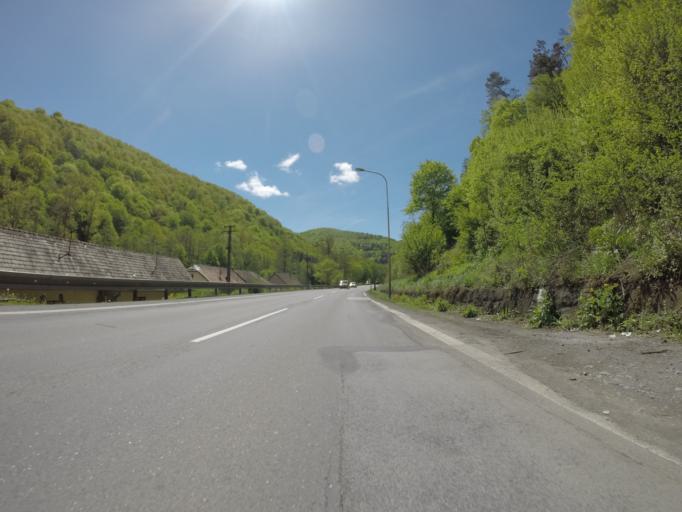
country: SK
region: Banskobystricky
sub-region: Okres Banska Bystrica
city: Zvolen
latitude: 48.5549
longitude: 19.1332
